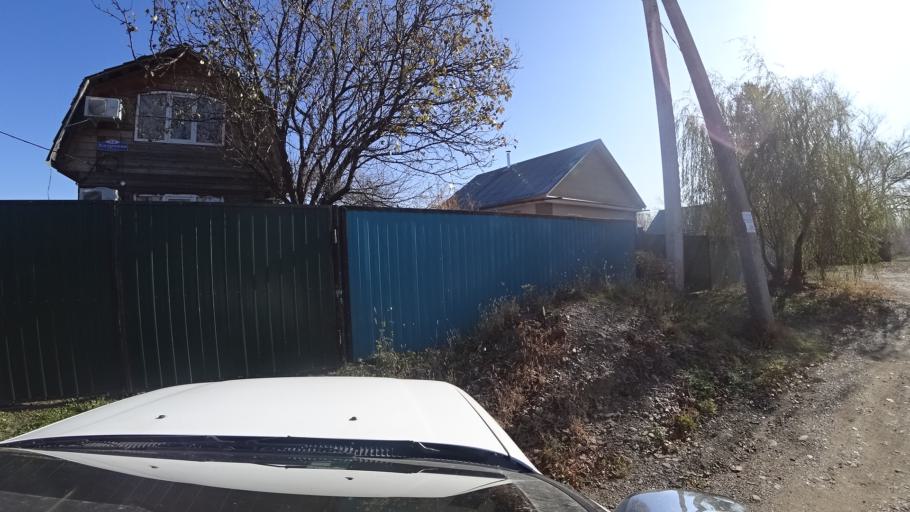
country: RU
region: Primorskiy
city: Dal'nerechensk
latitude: 45.9070
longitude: 133.8013
